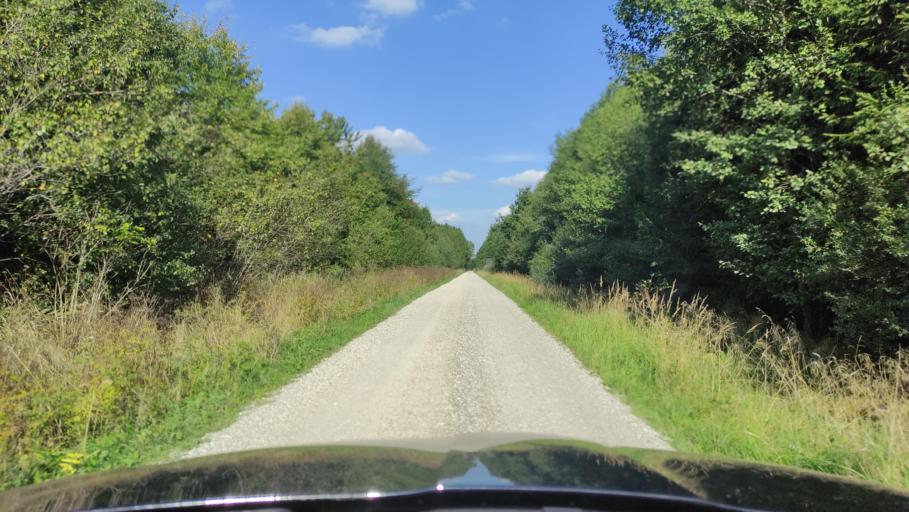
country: DE
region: Bavaria
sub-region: Swabia
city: Breitenthal
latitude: 48.2822
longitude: 10.2816
